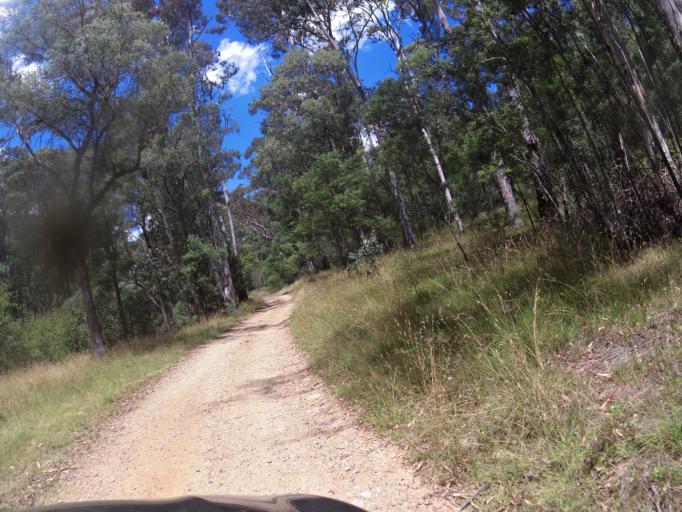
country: AU
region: Victoria
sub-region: Alpine
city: Mount Beauty
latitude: -36.7736
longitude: 147.0525
